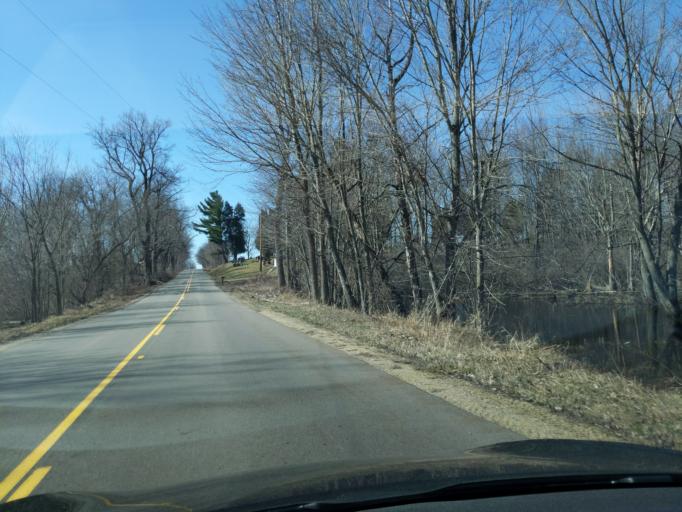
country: US
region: Michigan
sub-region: Ionia County
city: Lake Odessa
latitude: 42.7267
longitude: -84.9883
